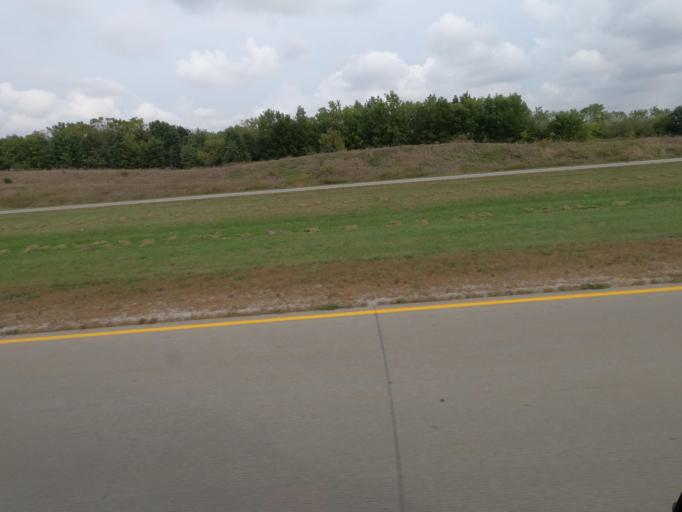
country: US
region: Iowa
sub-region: Wapello County
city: Ottumwa
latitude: 41.0681
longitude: -92.3933
